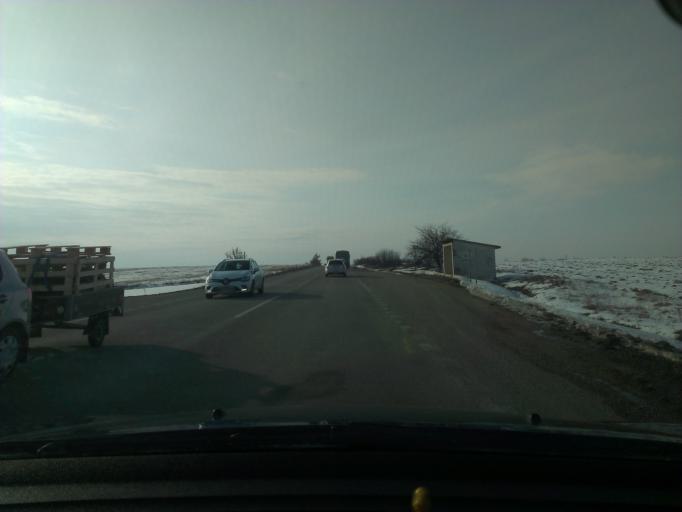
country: SK
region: Trenciansky
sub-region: Okres Myjava
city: Myjava
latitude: 48.7580
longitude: 17.6109
